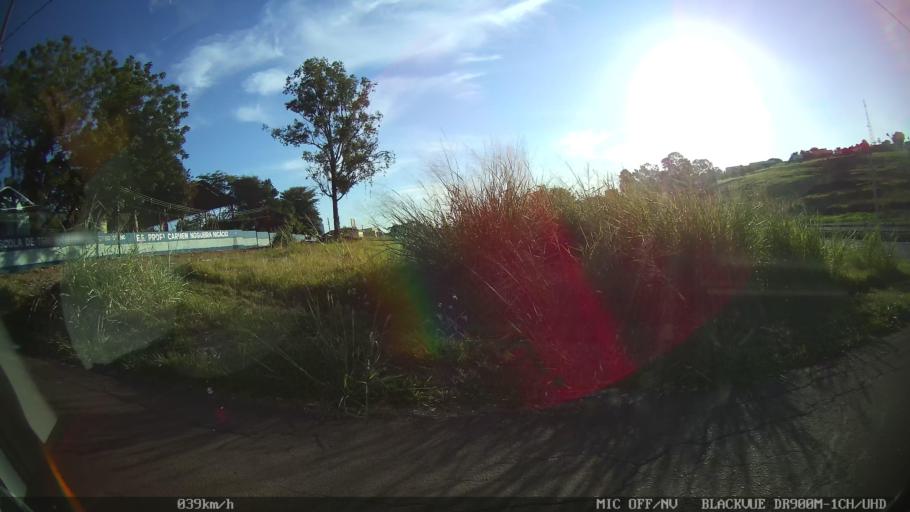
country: BR
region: Sao Paulo
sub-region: Franca
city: Franca
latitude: -20.5204
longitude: -47.3772
